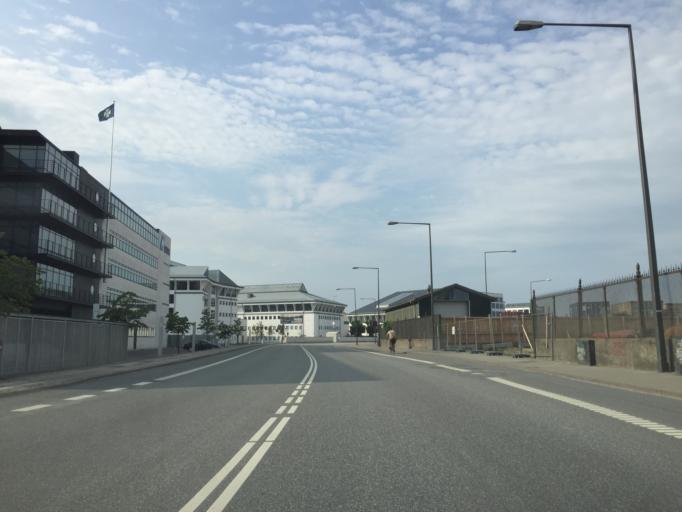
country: DK
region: Capital Region
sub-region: Kobenhavn
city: Christianshavn
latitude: 55.7109
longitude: 12.5933
